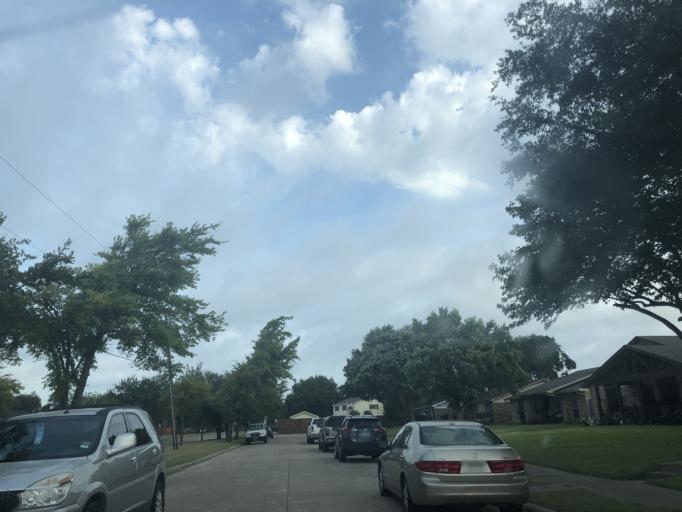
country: US
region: Texas
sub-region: Dallas County
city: Garland
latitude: 32.8438
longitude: -96.6268
